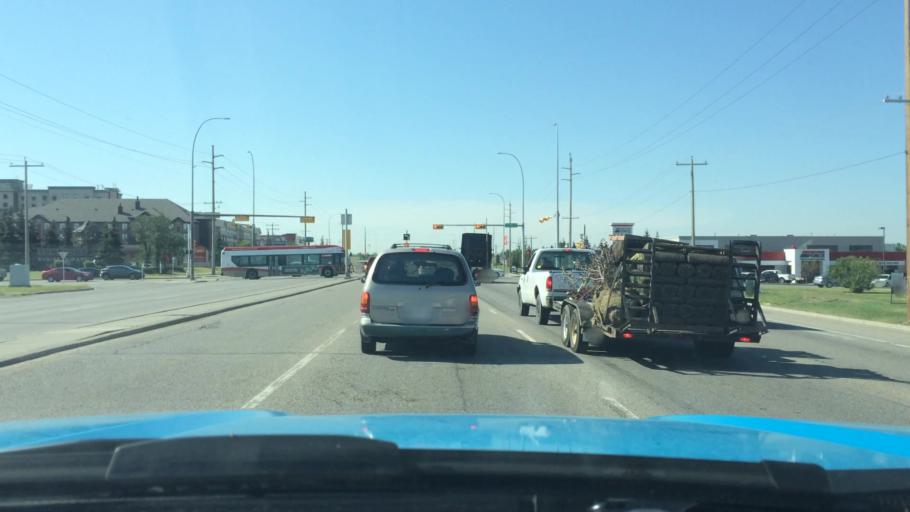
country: CA
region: Alberta
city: Calgary
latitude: 51.0742
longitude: -114.0017
